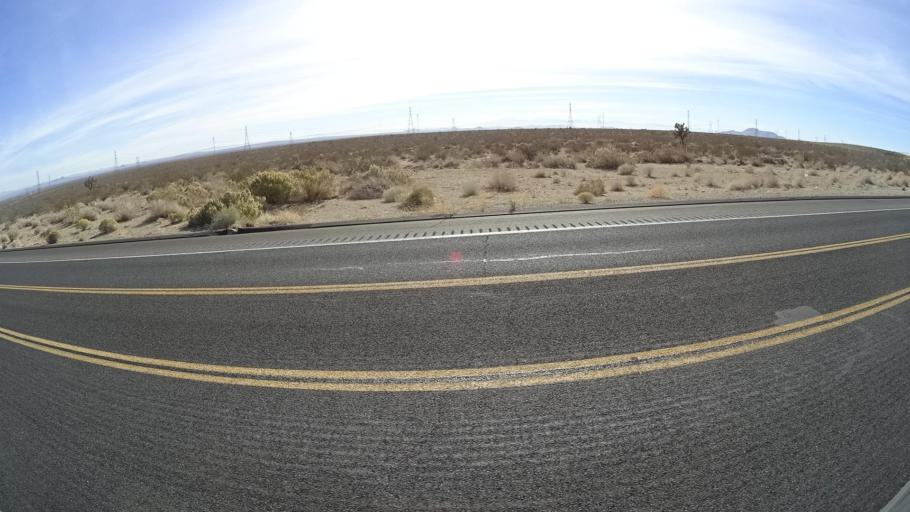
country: US
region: California
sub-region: Kern County
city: Mojave
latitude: 35.1237
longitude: -118.1732
